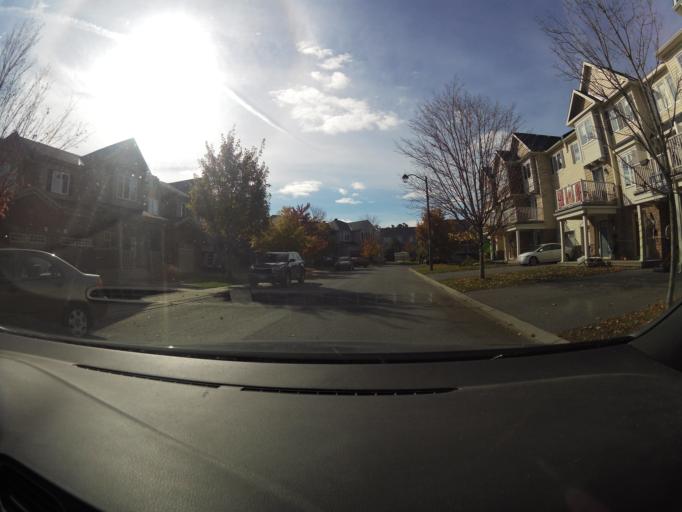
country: CA
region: Ontario
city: Bells Corners
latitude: 45.2880
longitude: -75.9231
